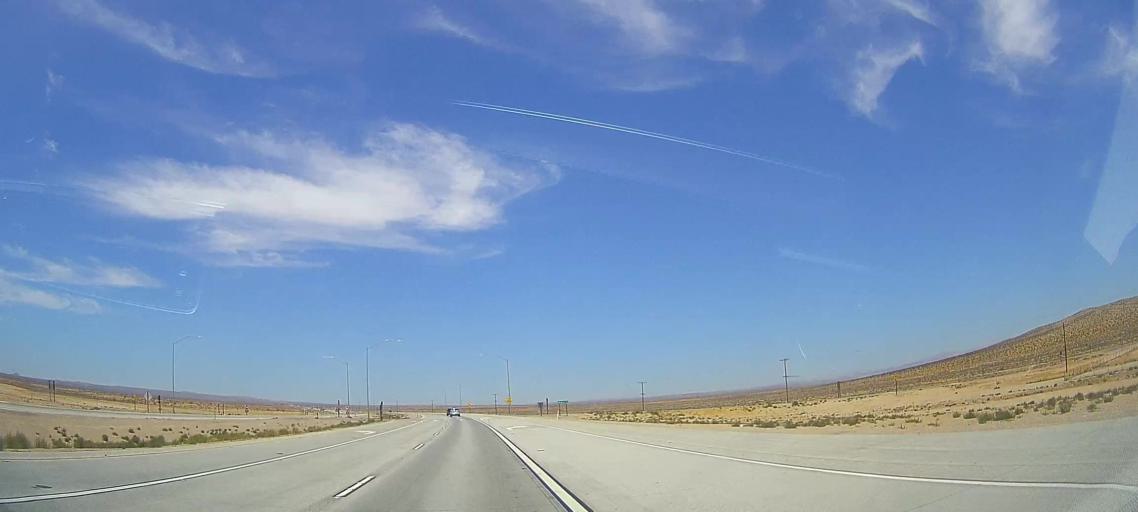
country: US
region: California
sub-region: San Bernardino County
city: Lenwood
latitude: 34.9214
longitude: -117.2515
